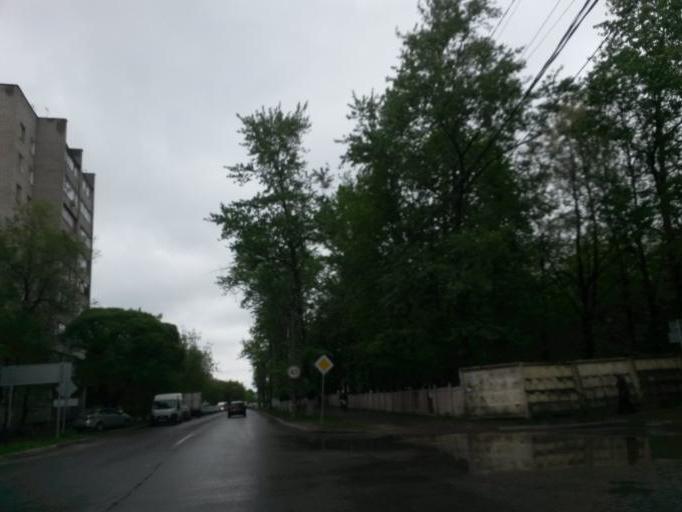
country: RU
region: Moskovskaya
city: Klimovsk
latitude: 55.3681
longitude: 37.5376
